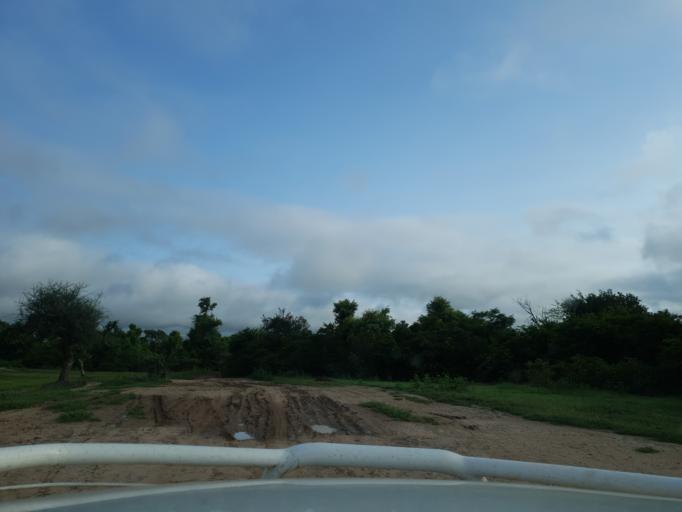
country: ML
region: Segou
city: Baroueli
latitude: 13.3891
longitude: -7.0064
